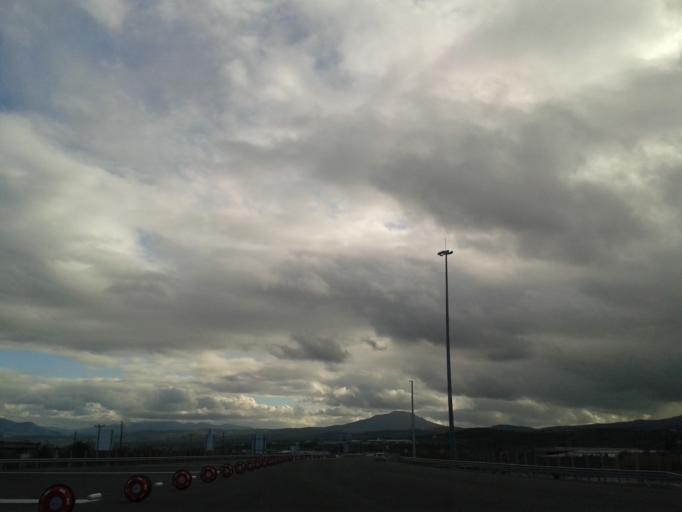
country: GR
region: Peloponnese
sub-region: Nomos Korinthias
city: Moulki
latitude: 37.9953
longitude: 22.7356
